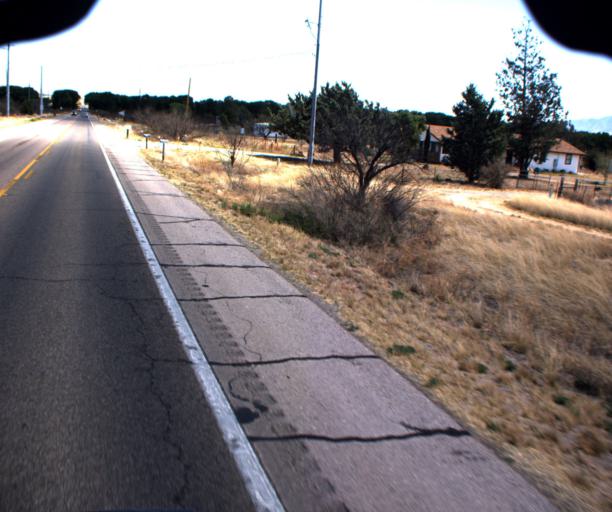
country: US
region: Arizona
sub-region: Cochise County
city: Sierra Vista Southeast
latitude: 31.3799
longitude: -110.1165
